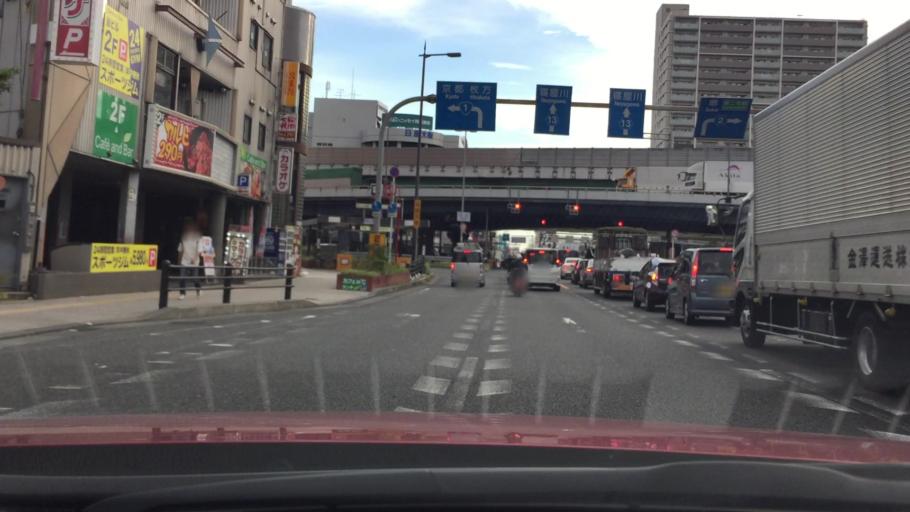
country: JP
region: Osaka
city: Kadoma
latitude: 34.7489
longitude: 135.5773
